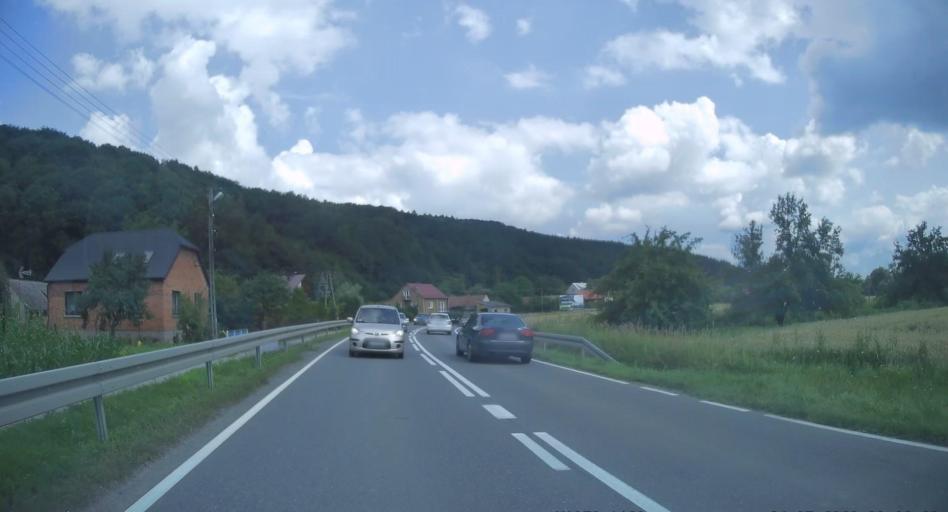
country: PL
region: Lesser Poland Voivodeship
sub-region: Powiat tarnowski
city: Wielka Wies
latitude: 49.9155
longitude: 20.8204
